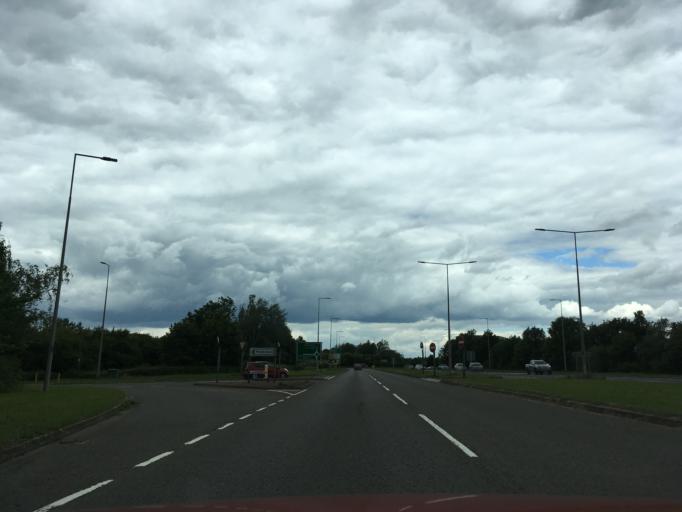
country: GB
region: England
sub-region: Milton Keynes
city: Broughton
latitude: 52.0381
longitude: -0.6928
